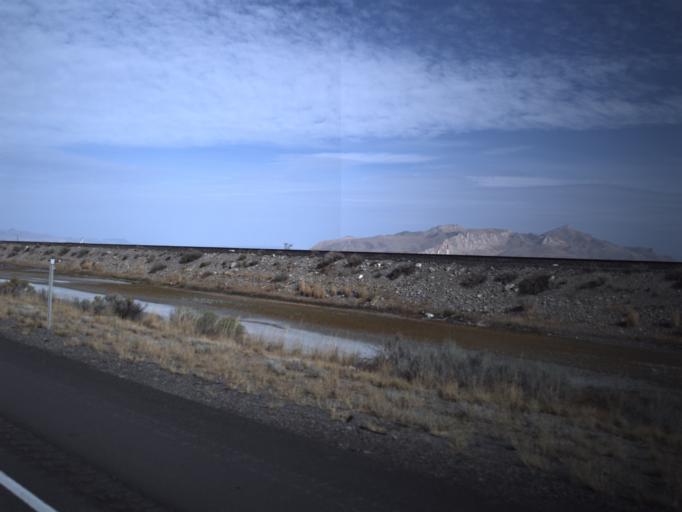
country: US
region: Utah
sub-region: Tooele County
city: Grantsville
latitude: 40.6793
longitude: -112.4136
